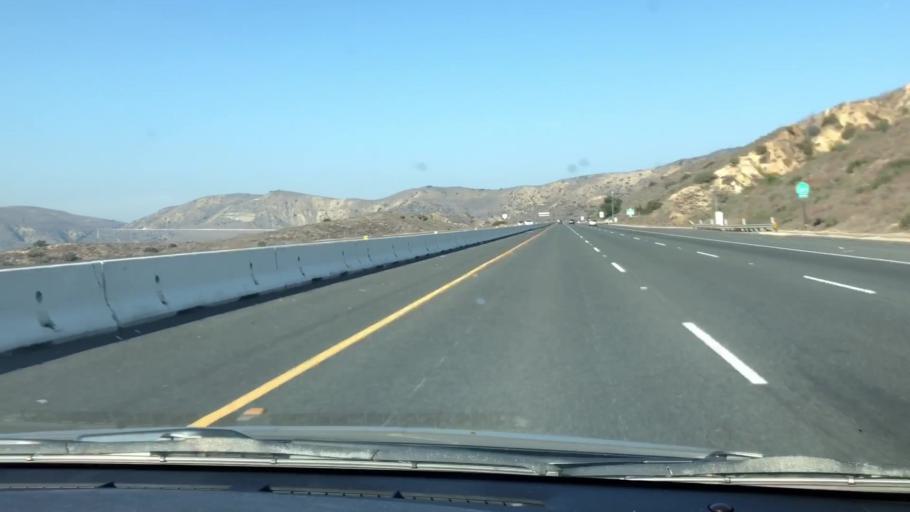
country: US
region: California
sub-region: Orange County
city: Foothill Ranch
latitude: 33.7274
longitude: -117.7189
